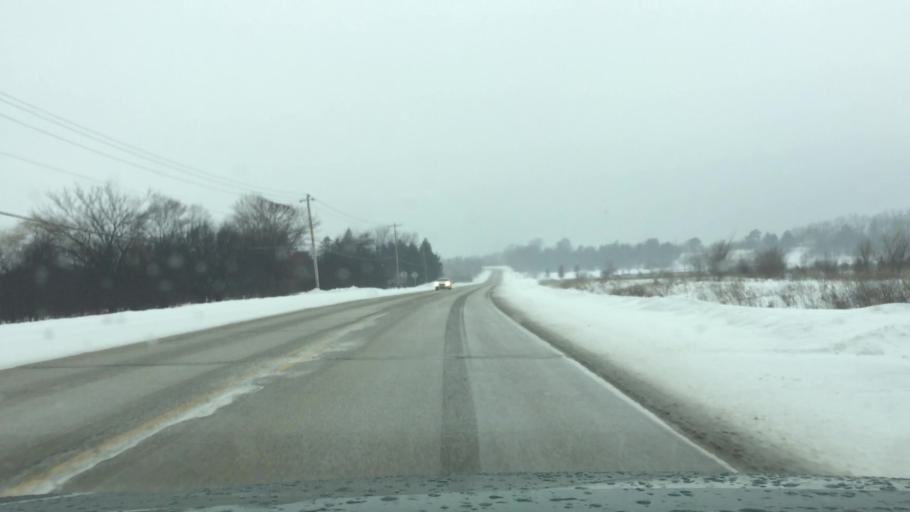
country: US
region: Wisconsin
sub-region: Waukesha County
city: North Prairie
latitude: 42.9310
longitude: -88.4145
